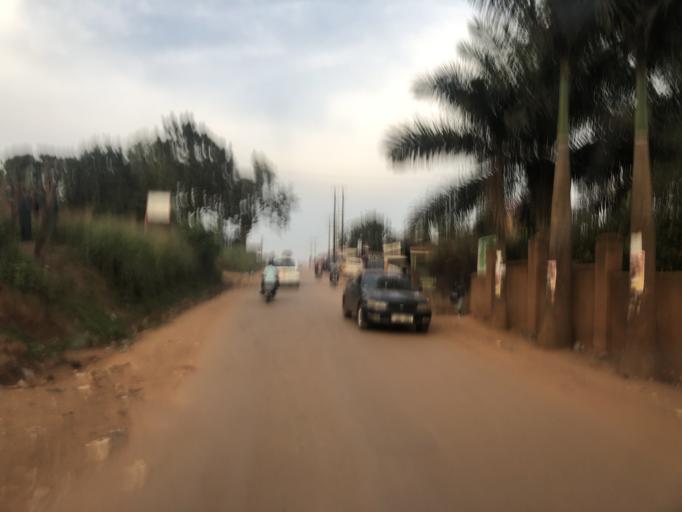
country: UG
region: Central Region
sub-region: Kampala District
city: Kampala
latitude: 0.2722
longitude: 32.5511
